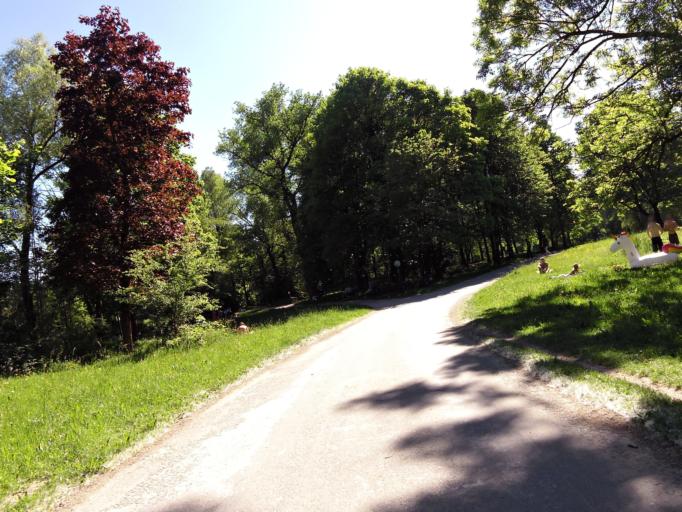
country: DE
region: Bavaria
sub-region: Upper Bavaria
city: Bogenhausen
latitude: 48.1626
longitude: 11.6098
